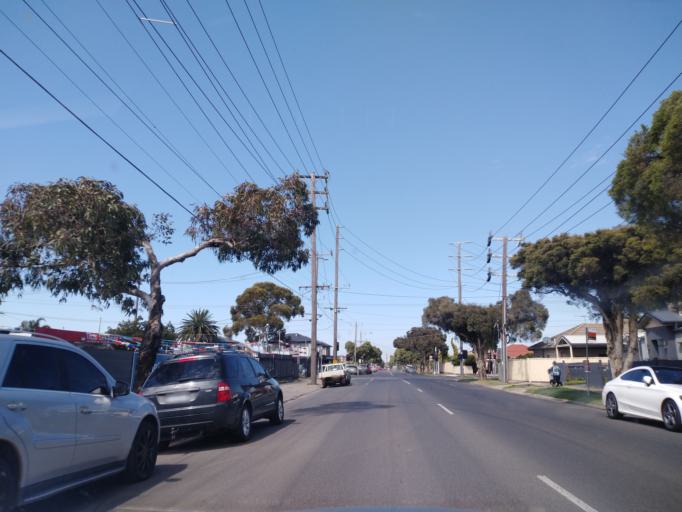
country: AU
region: Victoria
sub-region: Hobsons Bay
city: Altona North
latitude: -37.8314
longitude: 144.8565
